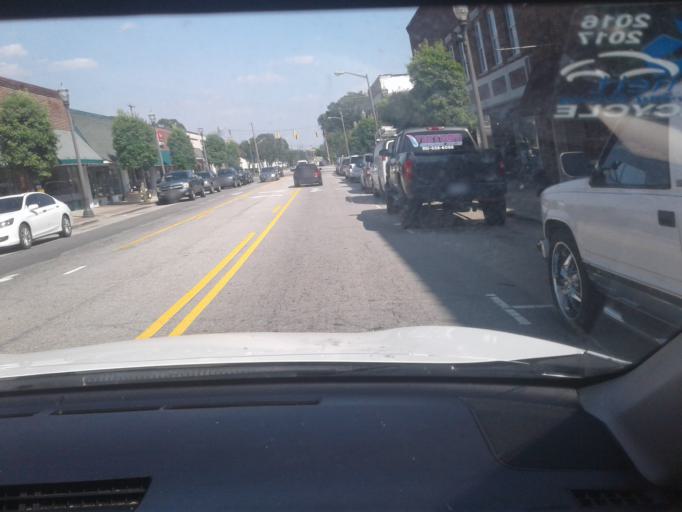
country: US
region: North Carolina
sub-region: Johnston County
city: Benson
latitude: 35.3807
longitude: -78.5467
